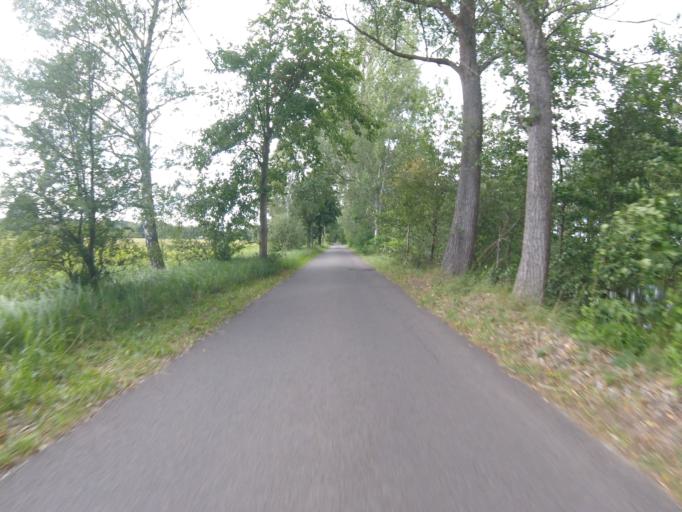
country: DE
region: Brandenburg
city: Halbe
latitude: 52.1015
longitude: 13.7699
